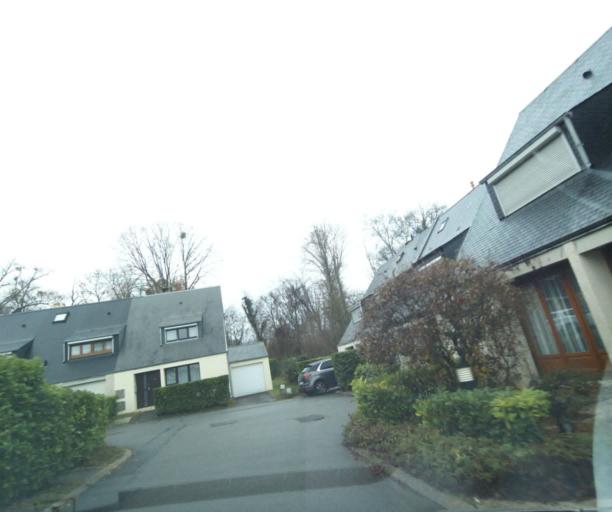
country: FR
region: Ile-de-France
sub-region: Departement de Seine-et-Marne
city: Avon
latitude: 48.4100
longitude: 2.7316
